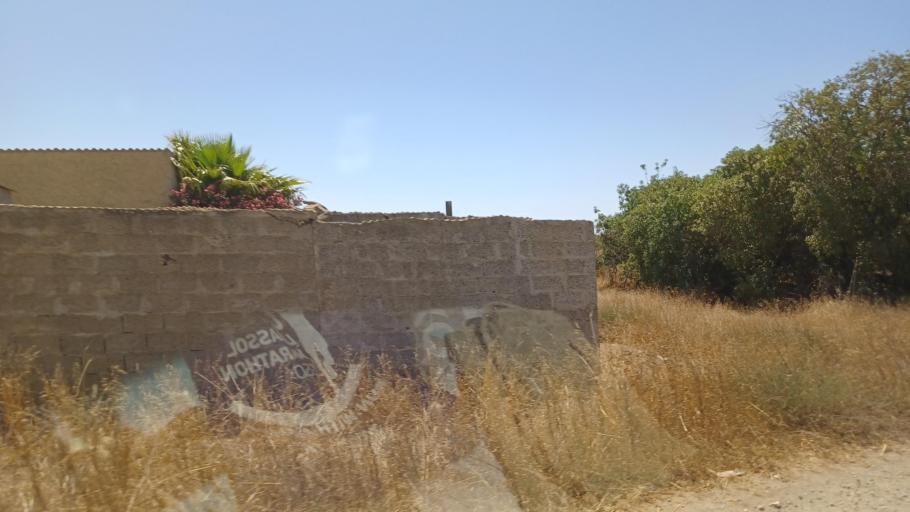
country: CY
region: Ammochostos
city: Avgorou
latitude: 35.0475
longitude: 33.8468
